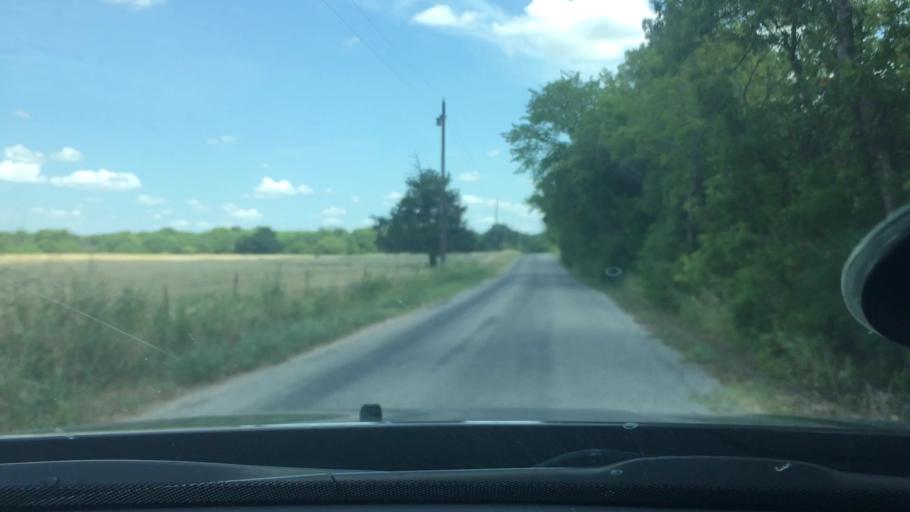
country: US
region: Oklahoma
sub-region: Love County
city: Marietta
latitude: 33.9985
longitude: -97.1870
